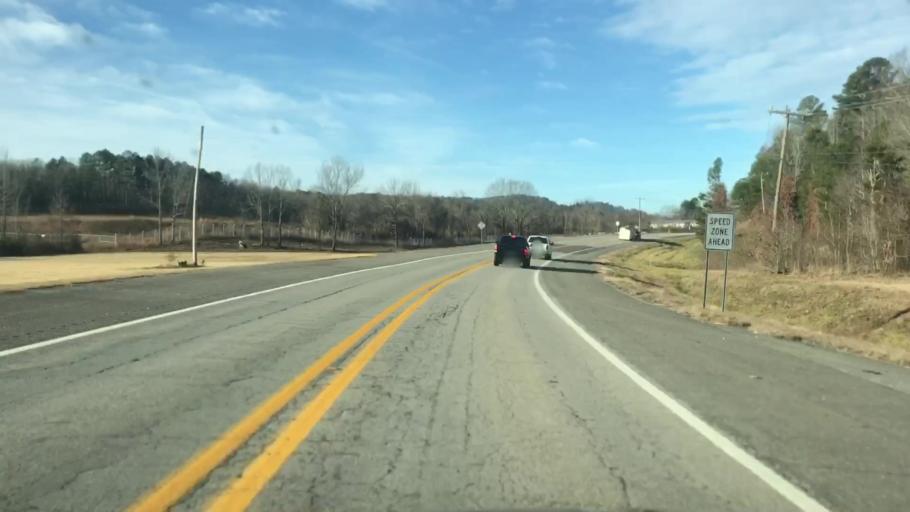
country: US
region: Arkansas
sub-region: Montgomery County
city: Mount Ida
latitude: 34.5318
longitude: -93.5216
